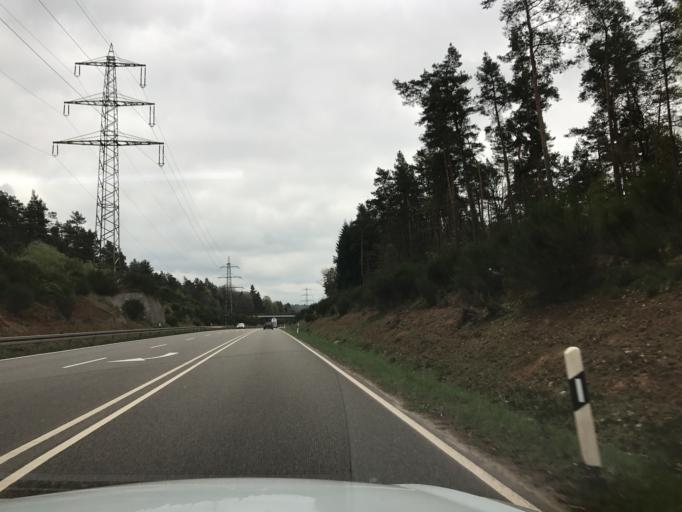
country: DE
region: Saarland
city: Mettlach
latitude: 49.4829
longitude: 6.6167
